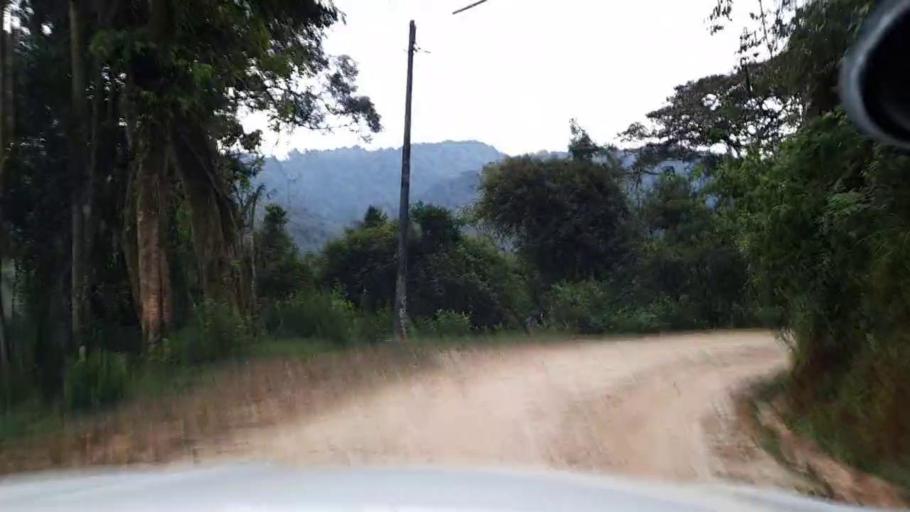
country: RW
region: Western Province
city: Cyangugu
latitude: -2.5618
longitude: 29.2282
